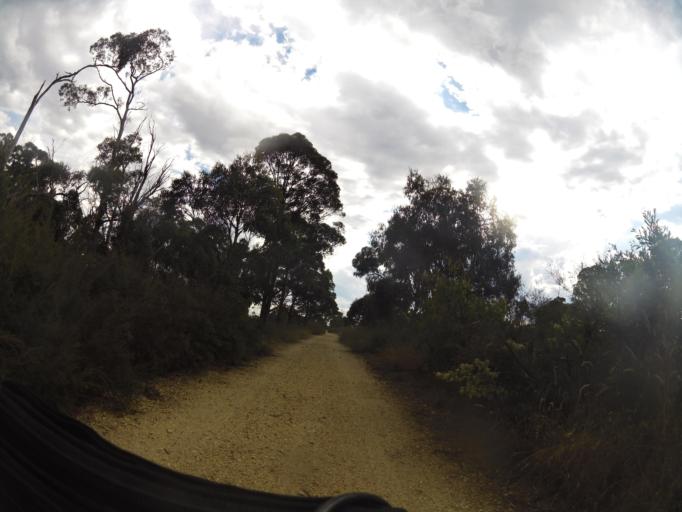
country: AU
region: Victoria
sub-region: Wellington
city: Heyfield
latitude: -38.0443
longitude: 146.6407
